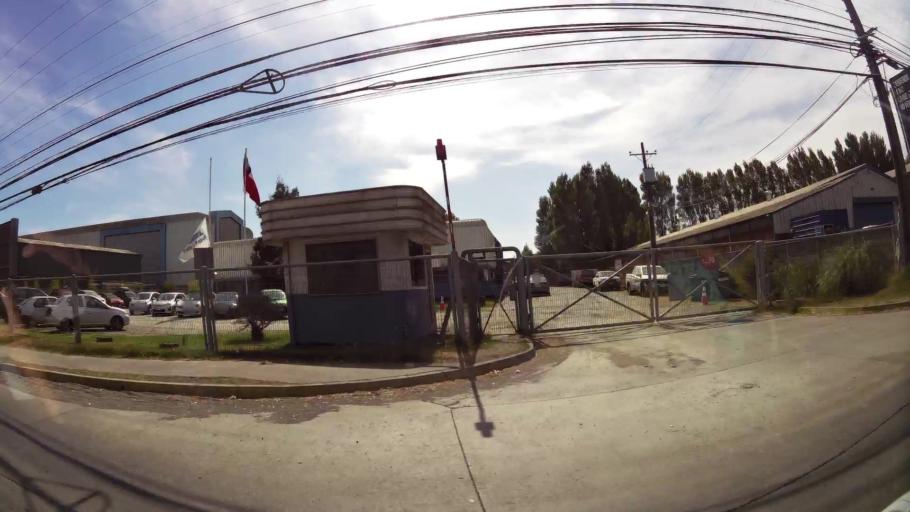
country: CL
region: Biobio
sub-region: Provincia de Concepcion
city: Talcahuano
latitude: -36.7688
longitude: -73.1151
